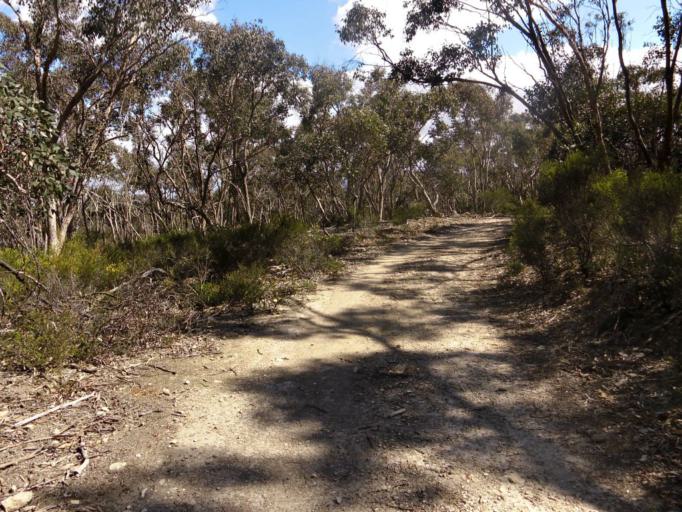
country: AU
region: Victoria
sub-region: Moorabool
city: Bacchus Marsh
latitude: -37.6640
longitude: 144.5030
